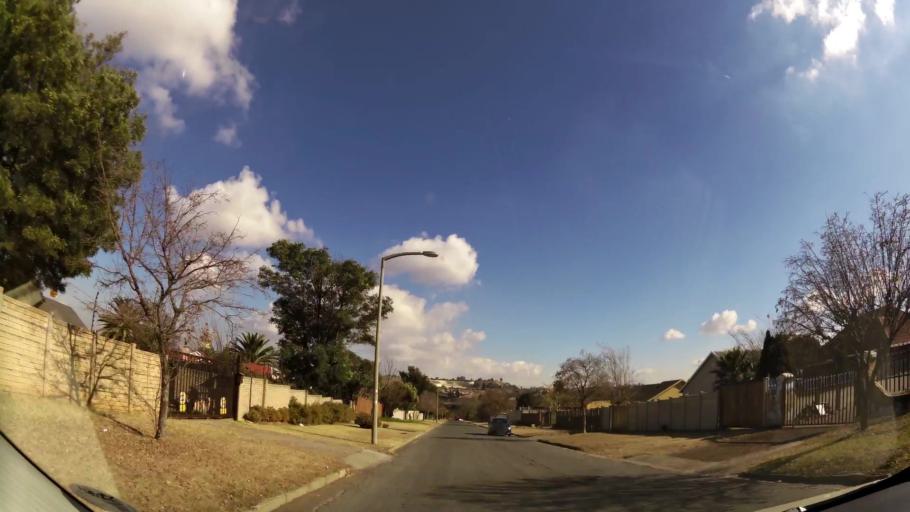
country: ZA
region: Gauteng
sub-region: City of Johannesburg Metropolitan Municipality
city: Roodepoort
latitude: -26.1457
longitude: 27.8242
